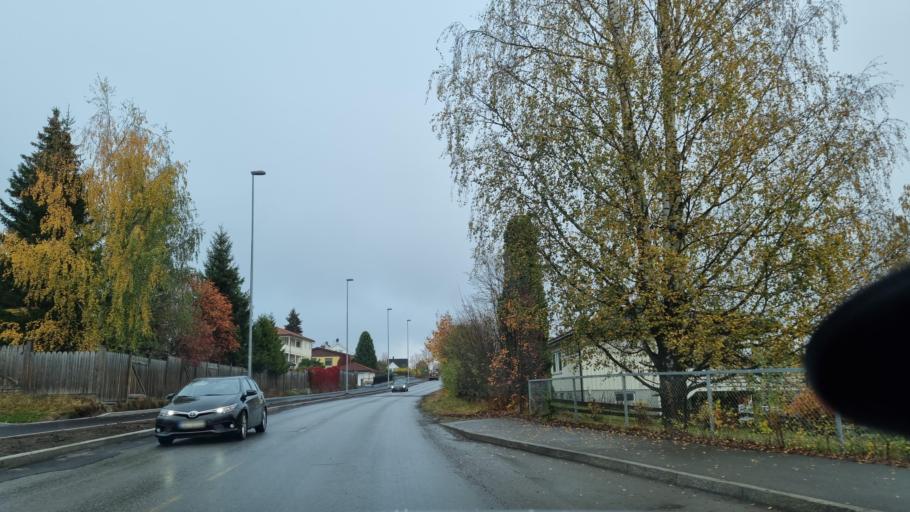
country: NO
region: Hedmark
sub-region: Hamar
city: Hamar
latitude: 60.8051
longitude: 11.0586
